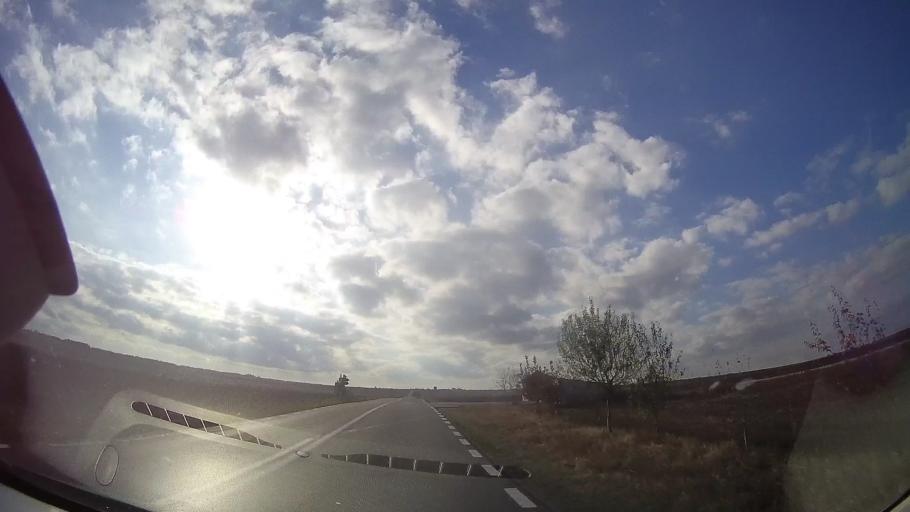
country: RO
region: Constanta
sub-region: Comuna Albesti
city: Albesti
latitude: 43.8208
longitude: 28.4705
